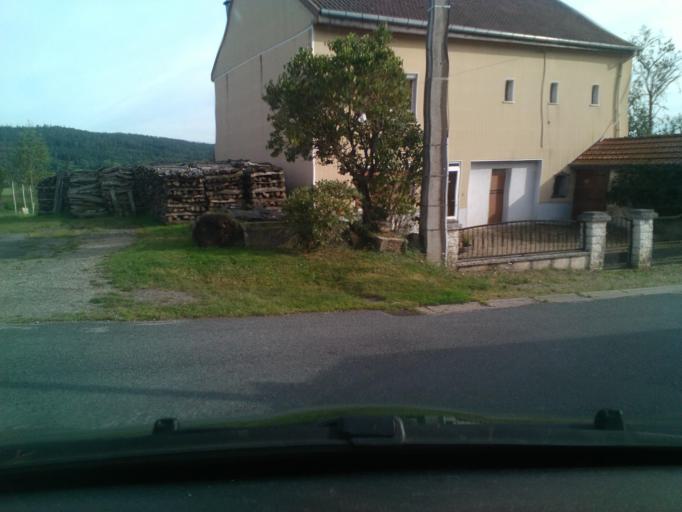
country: FR
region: Lorraine
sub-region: Departement des Vosges
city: Corcieux
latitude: 48.2022
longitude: 6.8812
